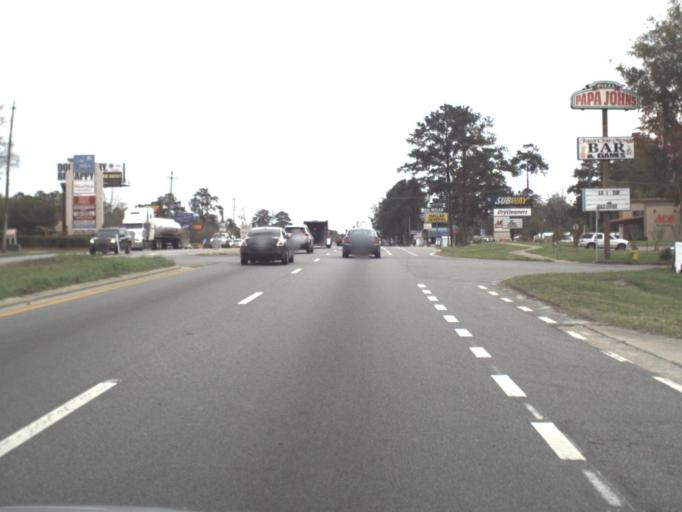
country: US
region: Florida
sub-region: Leon County
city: Tallahassee
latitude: 30.5018
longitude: -84.3290
